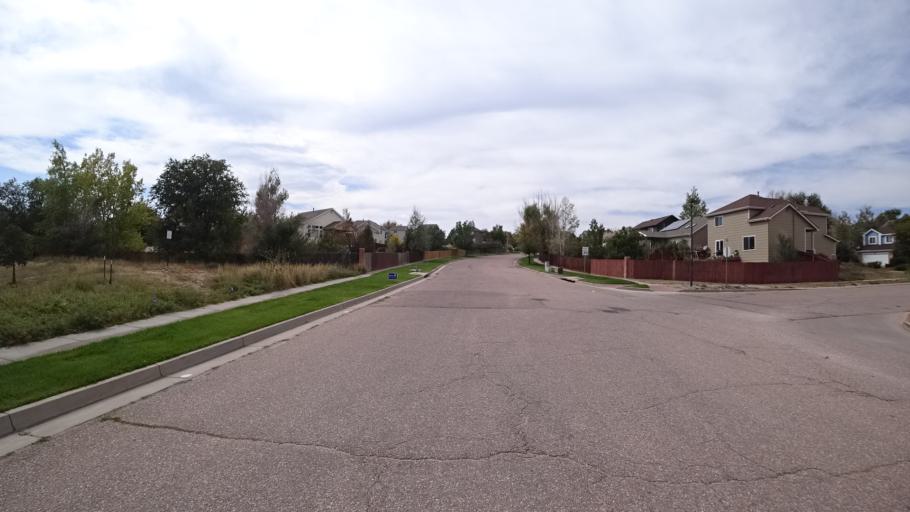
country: US
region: Colorado
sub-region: El Paso County
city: Cimarron Hills
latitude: 38.8994
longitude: -104.7110
